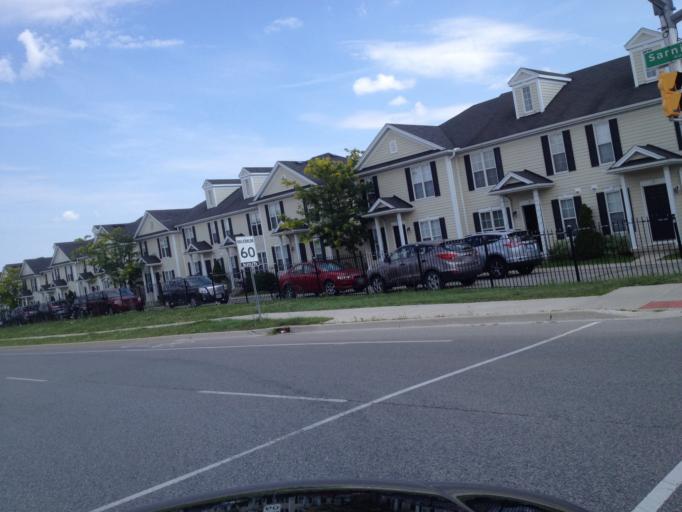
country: CA
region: Ontario
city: London
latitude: 42.9930
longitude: -81.3075
